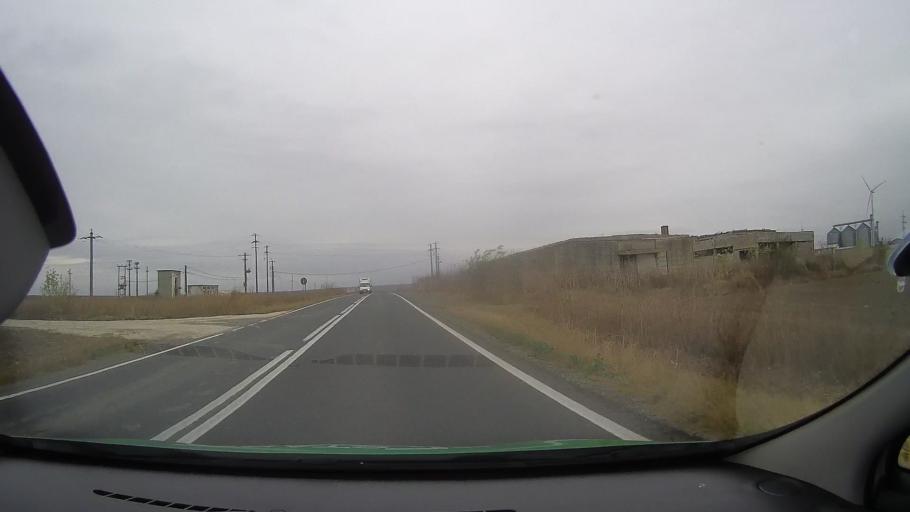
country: RO
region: Constanta
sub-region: Comuna Nicolae Balcescu
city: Dorobantu
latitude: 44.4225
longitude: 28.3110
